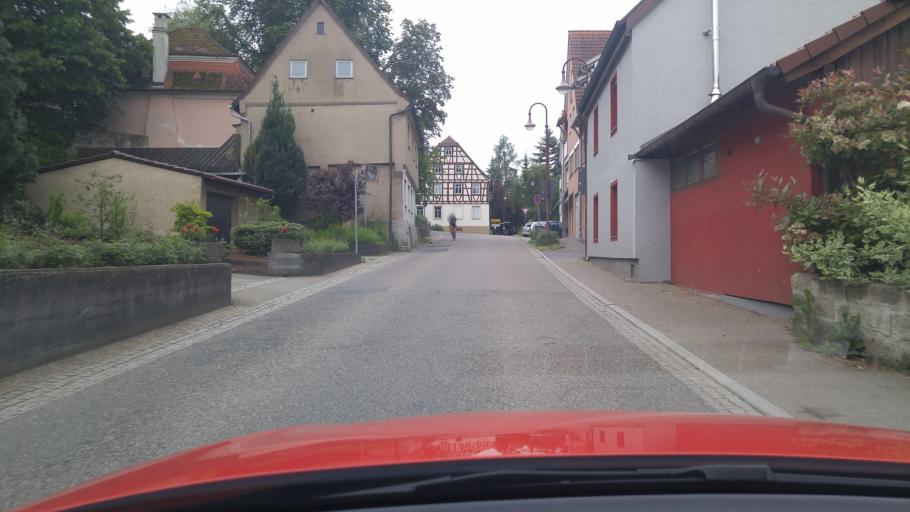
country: DE
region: Baden-Wuerttemberg
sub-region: Regierungsbezirk Stuttgart
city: Lowenstein
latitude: 49.1381
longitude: 9.4030
